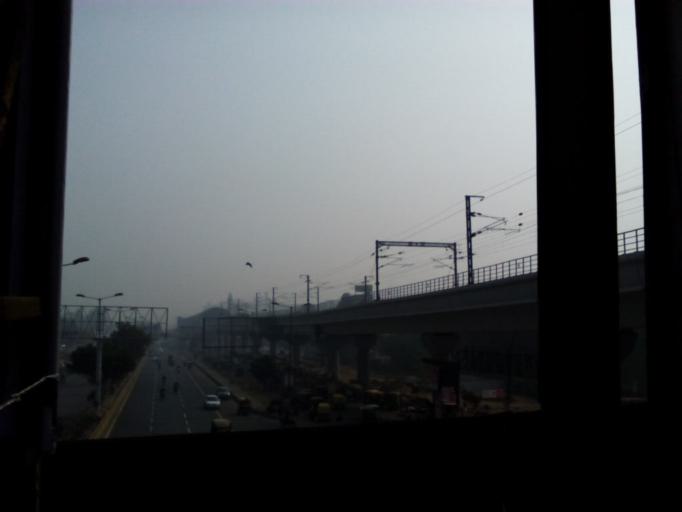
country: IN
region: Uttar Pradesh
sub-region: Gautam Buddha Nagar
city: Noida
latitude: 28.6455
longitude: 77.3197
